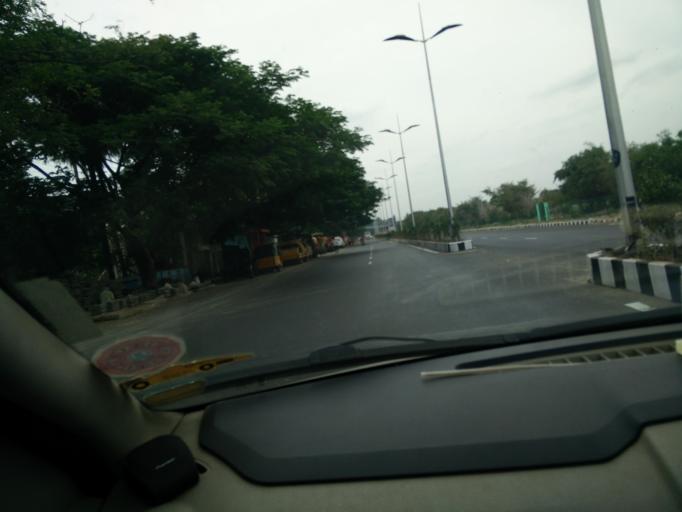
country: IN
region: Tamil Nadu
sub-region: Chennai
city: Chennai
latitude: 13.0691
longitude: 80.2786
